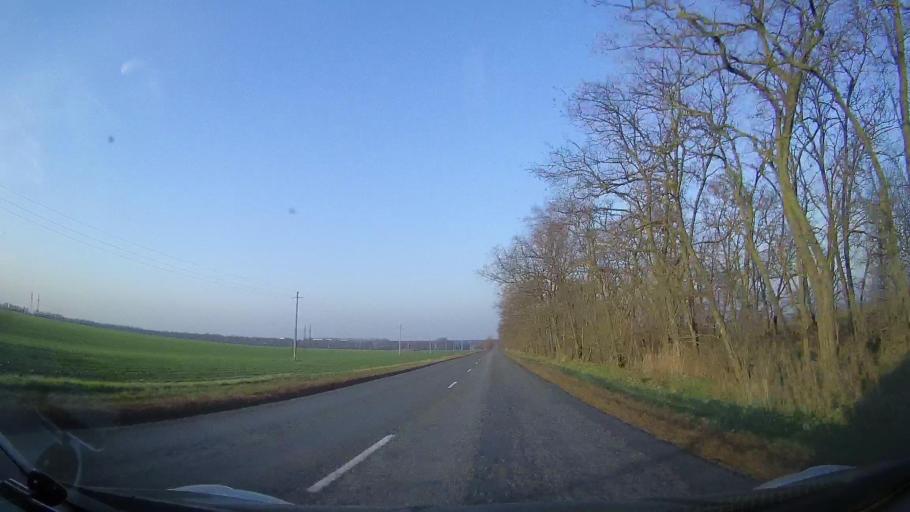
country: RU
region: Rostov
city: Ol'ginskaya
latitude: 47.1034
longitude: 39.9776
